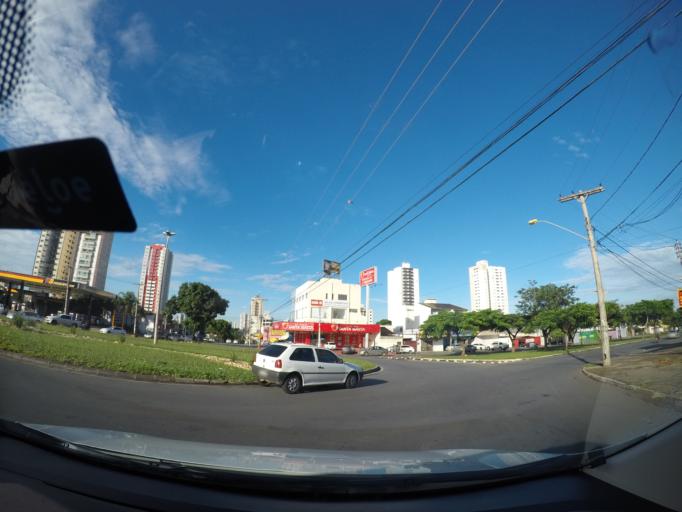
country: BR
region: Goias
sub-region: Goiania
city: Goiania
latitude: -16.7241
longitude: -49.2701
